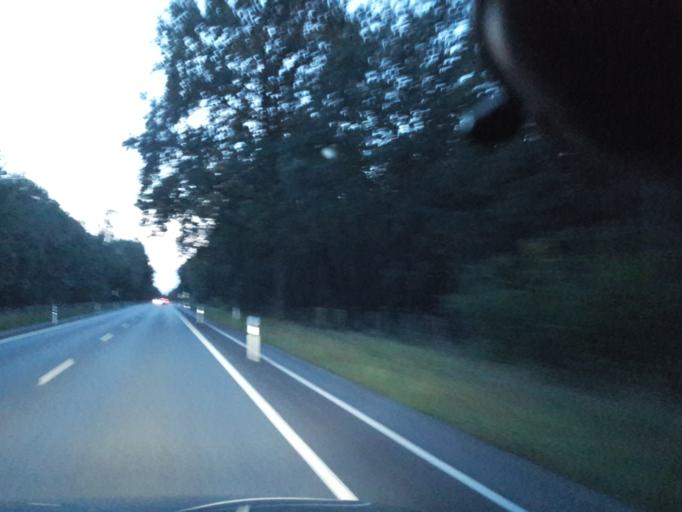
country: DE
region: North Rhine-Westphalia
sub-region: Regierungsbezirk Dusseldorf
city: Schermbeck
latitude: 51.7314
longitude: 6.8996
